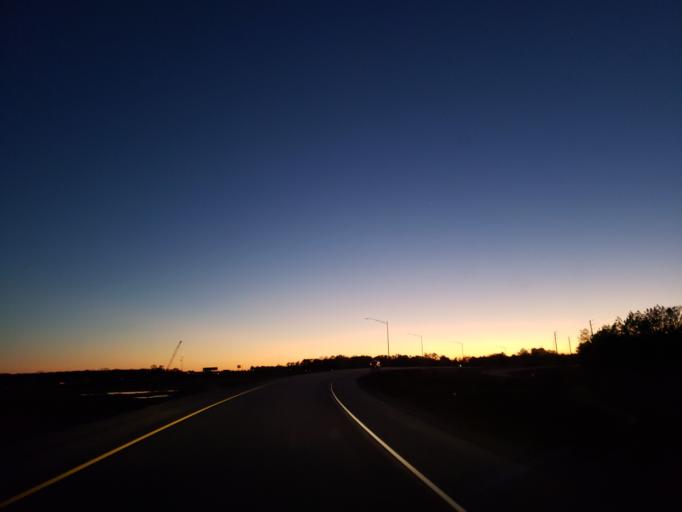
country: US
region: Mississippi
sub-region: Forrest County
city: Glendale
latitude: 31.3865
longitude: -89.3219
